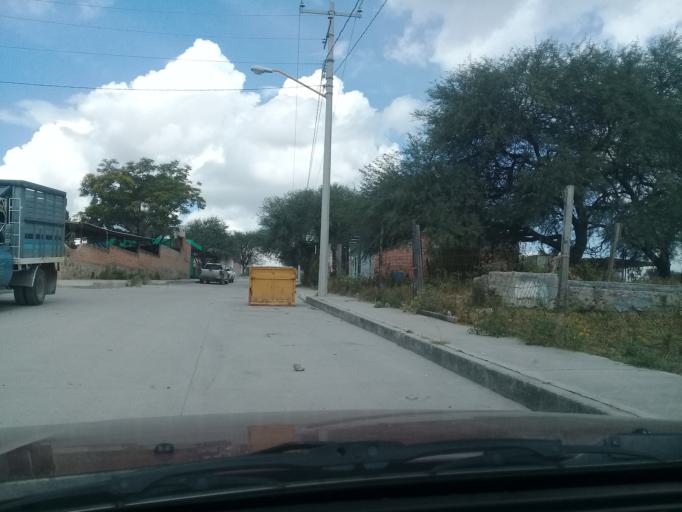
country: MX
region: Aguascalientes
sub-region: Aguascalientes
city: Penuelas (El Cienegal)
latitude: 21.7724
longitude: -102.3106
